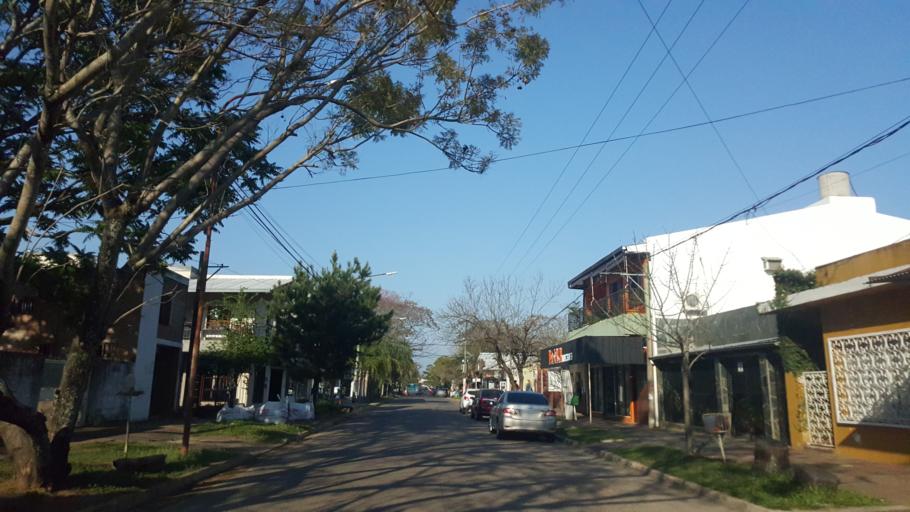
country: AR
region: Corrientes
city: Ituzaingo
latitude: -27.5832
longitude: -56.6858
